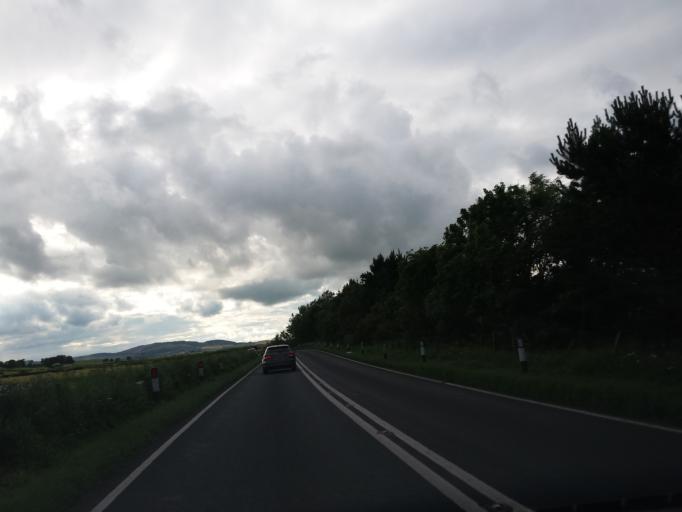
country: GB
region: Scotland
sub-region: Fife
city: Strathkinness
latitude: 56.3505
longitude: -2.8398
